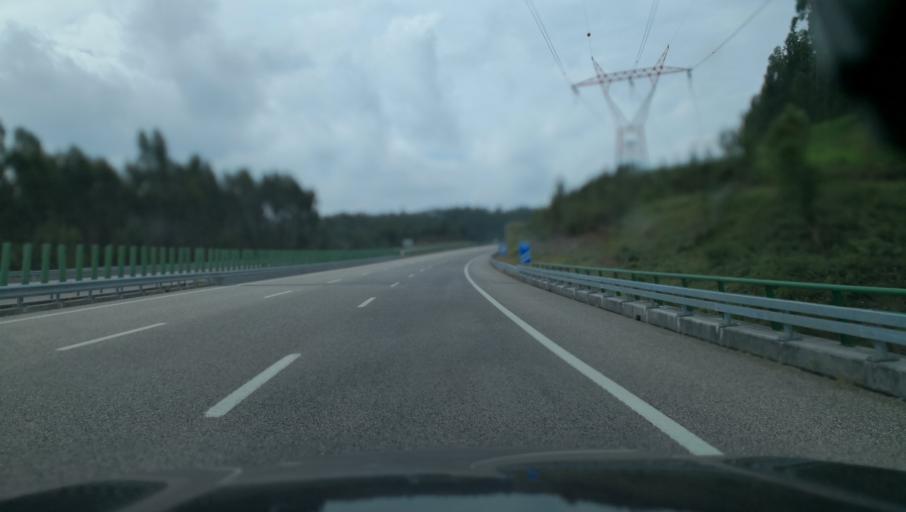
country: PT
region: Leiria
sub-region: Pombal
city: Lourical
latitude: 39.9530
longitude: -8.7724
